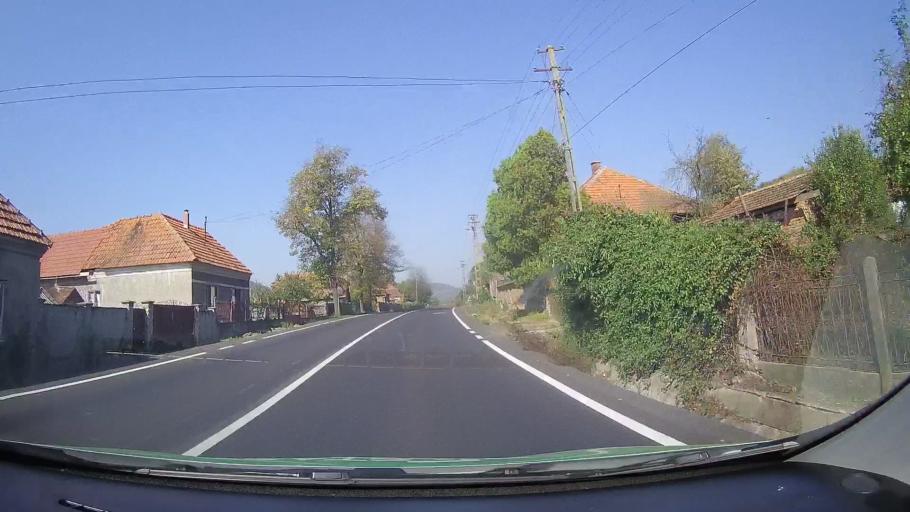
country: RO
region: Hunedoara
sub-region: Comuna Burjuc
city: Burjuc
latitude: 45.9477
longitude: 22.4923
